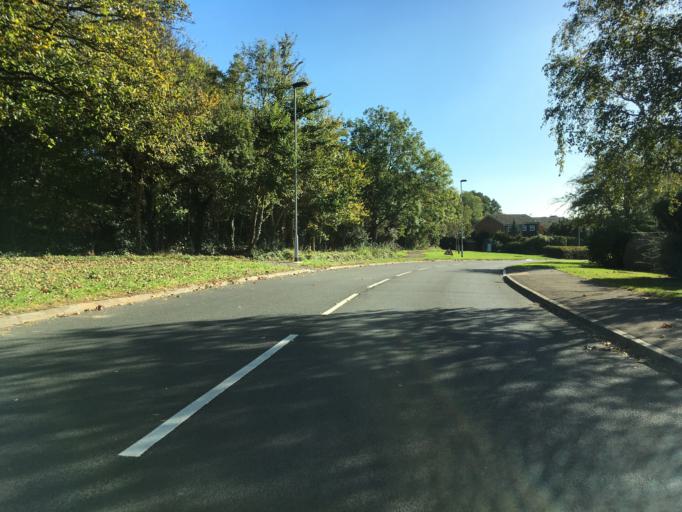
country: GB
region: England
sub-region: South Gloucestershire
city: Chipping Sodbury
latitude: 51.5492
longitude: -2.4027
